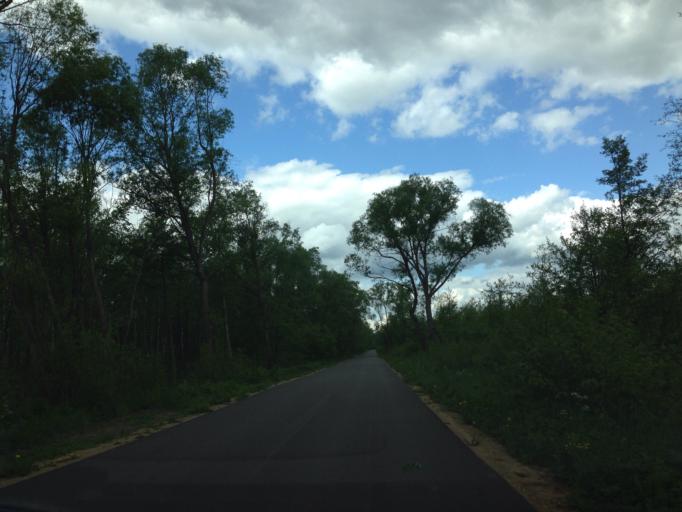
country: PL
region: Podlasie
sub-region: Powiat bialostocki
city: Tykocin
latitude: 53.3130
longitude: 22.6027
